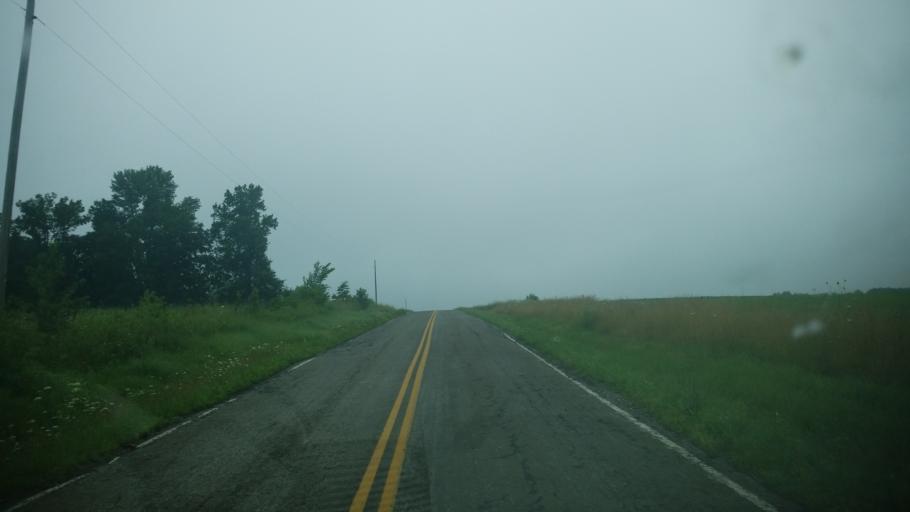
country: US
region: Missouri
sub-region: Audrain County
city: Vandalia
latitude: 39.2830
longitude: -91.3462
